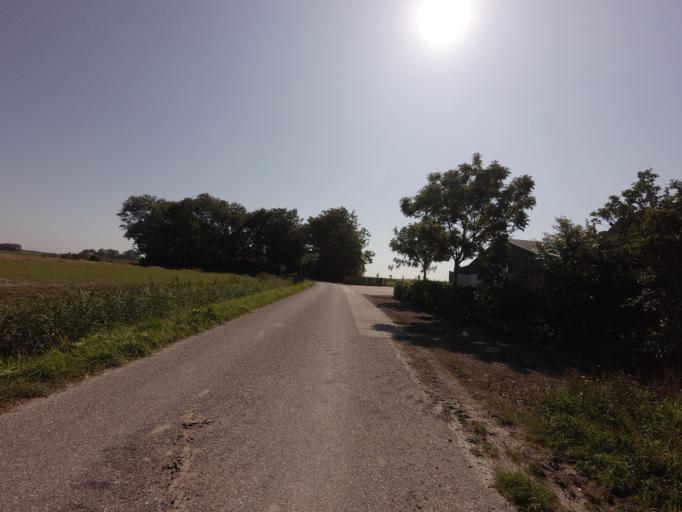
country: NL
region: Friesland
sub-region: Gemeente Dongeradeel
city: Holwerd
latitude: 53.3669
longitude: 5.9240
